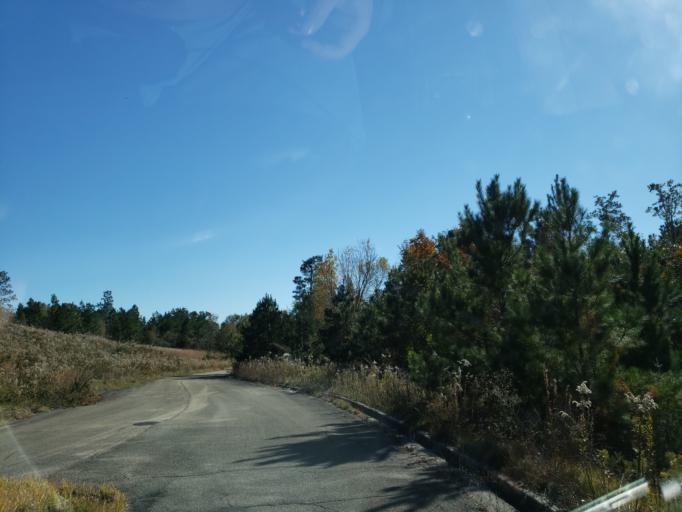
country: US
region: Mississippi
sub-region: Lamar County
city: West Hattiesburg
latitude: 31.3001
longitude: -89.3601
